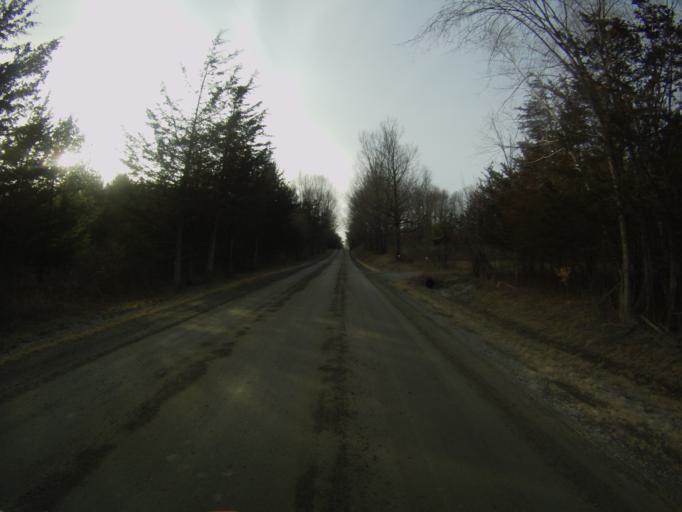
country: US
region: Vermont
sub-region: Addison County
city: Middlebury (village)
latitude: 44.0370
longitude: -73.2734
